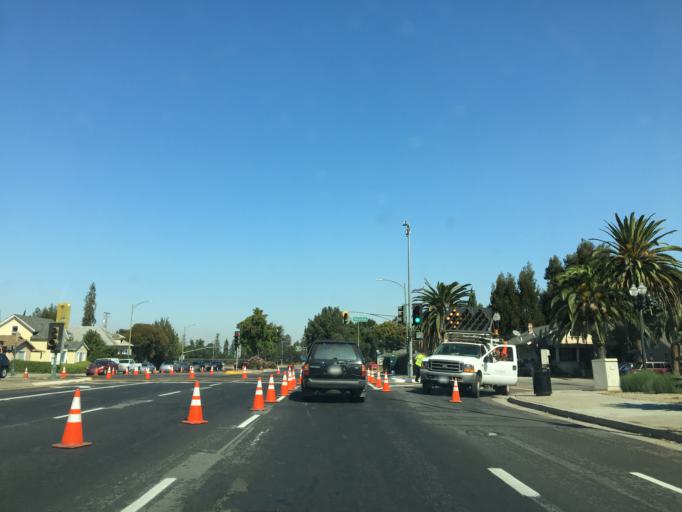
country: US
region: California
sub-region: Santa Clara County
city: Buena Vista
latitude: 37.3197
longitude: -121.8975
